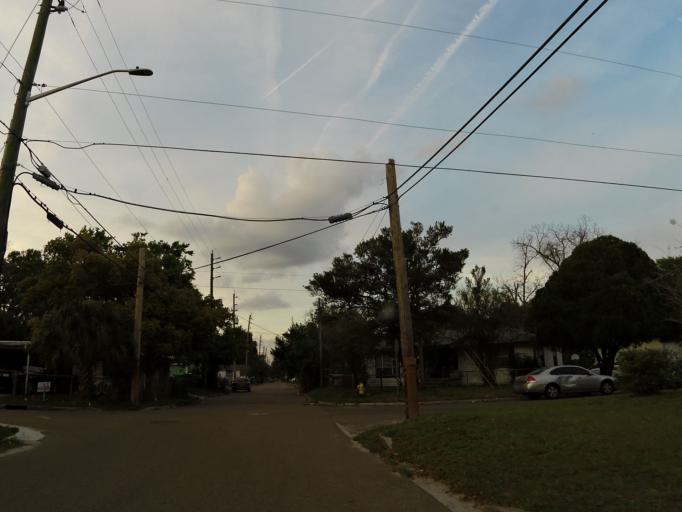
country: US
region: Florida
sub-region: Duval County
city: Jacksonville
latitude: 30.3586
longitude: -81.6371
